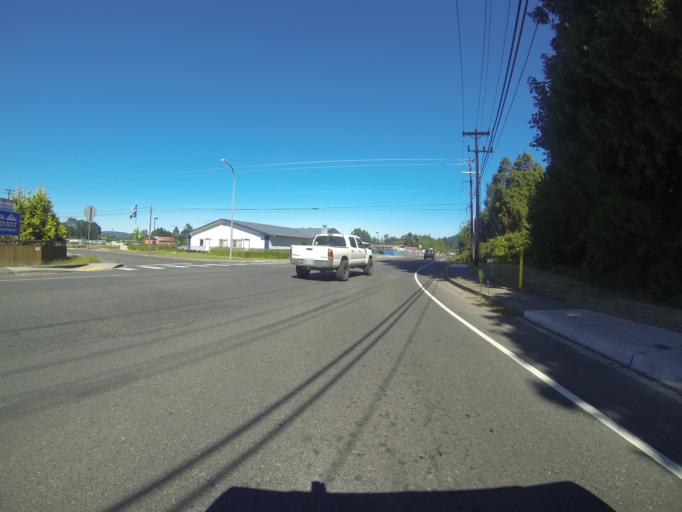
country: US
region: Washington
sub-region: Cowlitz County
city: Woodland
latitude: 45.9178
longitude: -122.7441
